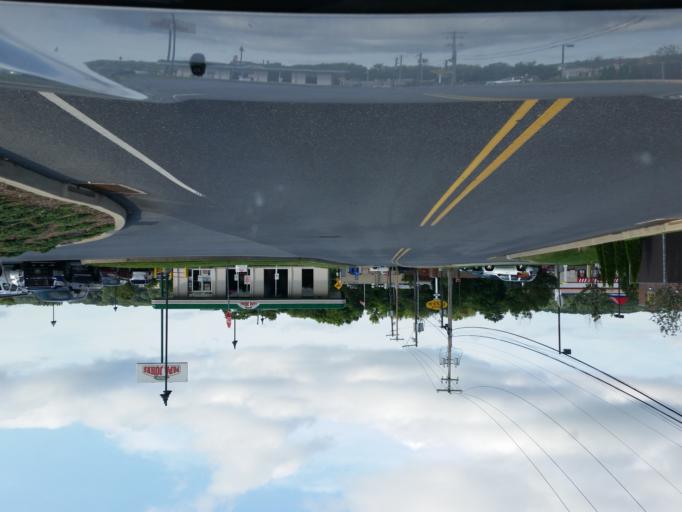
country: US
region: Pennsylvania
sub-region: Dauphin County
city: Hummelstown
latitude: 40.2684
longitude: -76.6906
